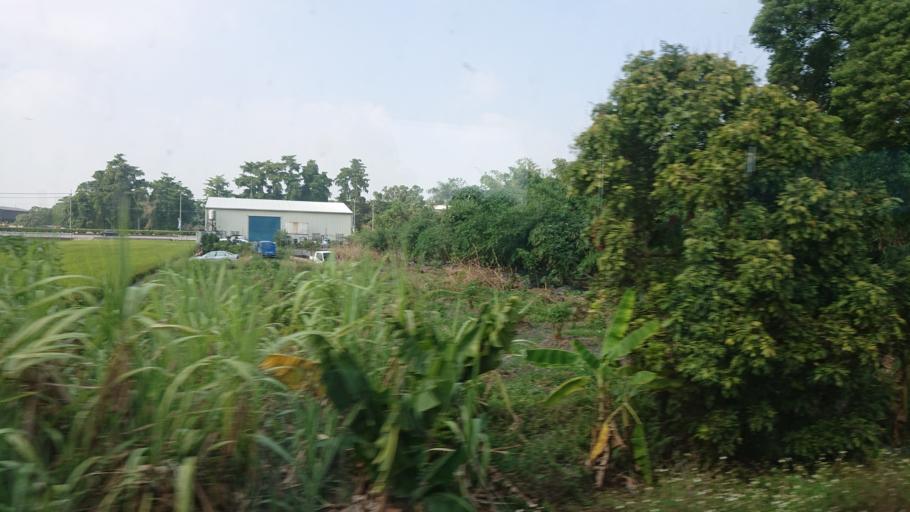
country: TW
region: Taiwan
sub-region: Yunlin
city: Douliu
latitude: 23.6373
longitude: 120.4706
